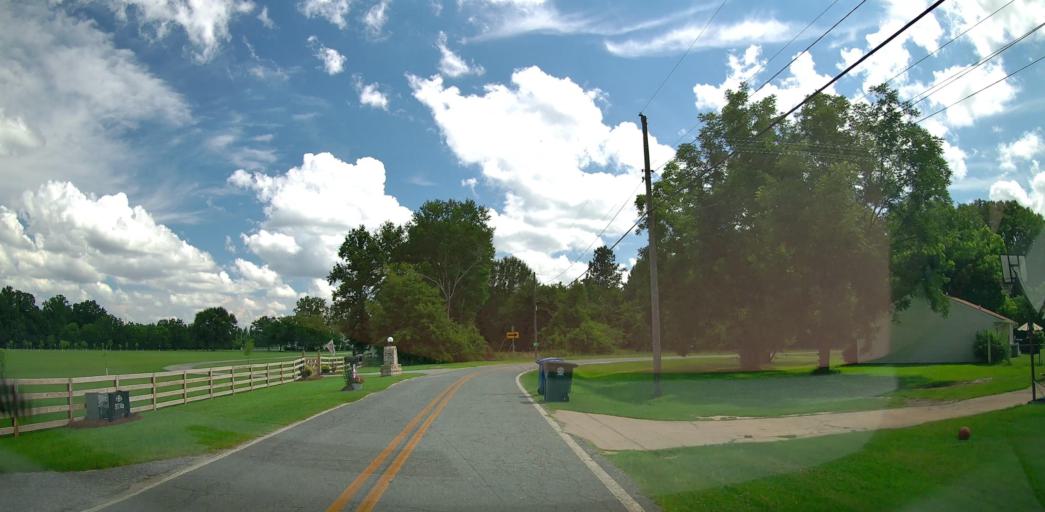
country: US
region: Georgia
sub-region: Houston County
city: Centerville
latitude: 32.7046
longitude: -83.6793
